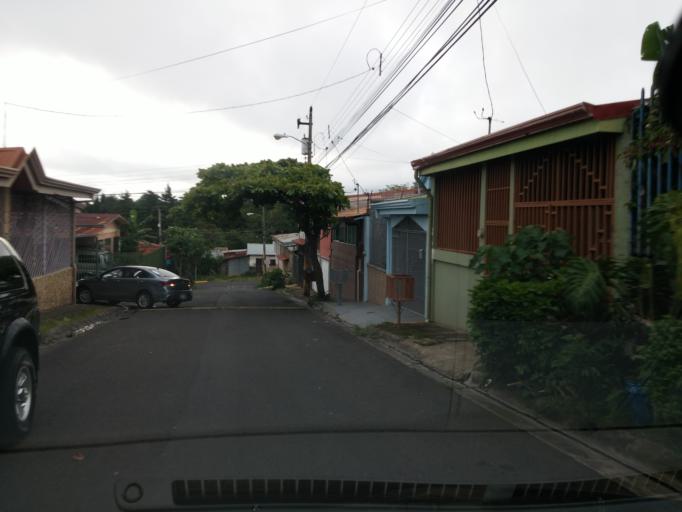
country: CR
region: Heredia
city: San Josecito
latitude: 10.0223
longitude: -84.1037
